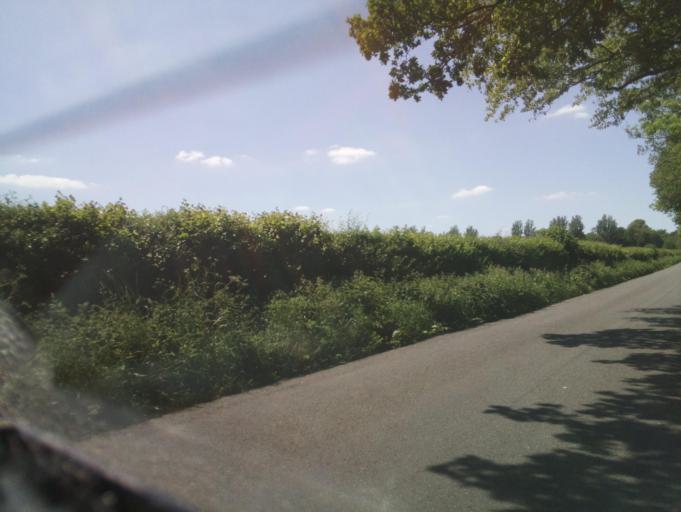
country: GB
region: England
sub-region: Wiltshire
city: Lyneham
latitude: 51.4720
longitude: -1.9724
